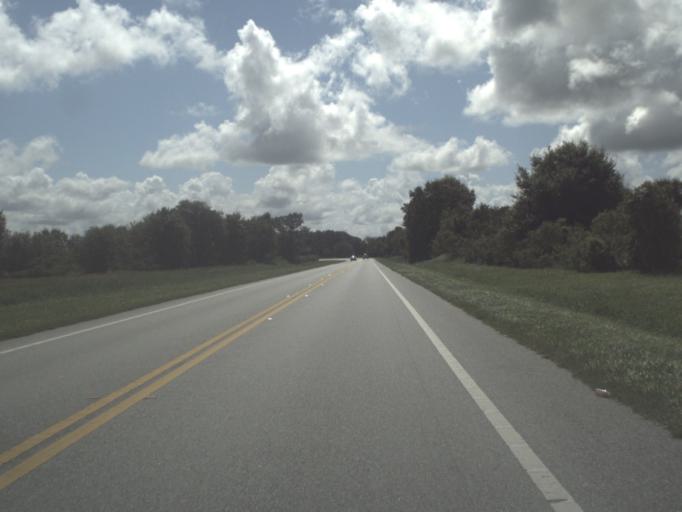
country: US
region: Florida
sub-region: DeSoto County
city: Arcadia
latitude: 27.3329
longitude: -82.1347
